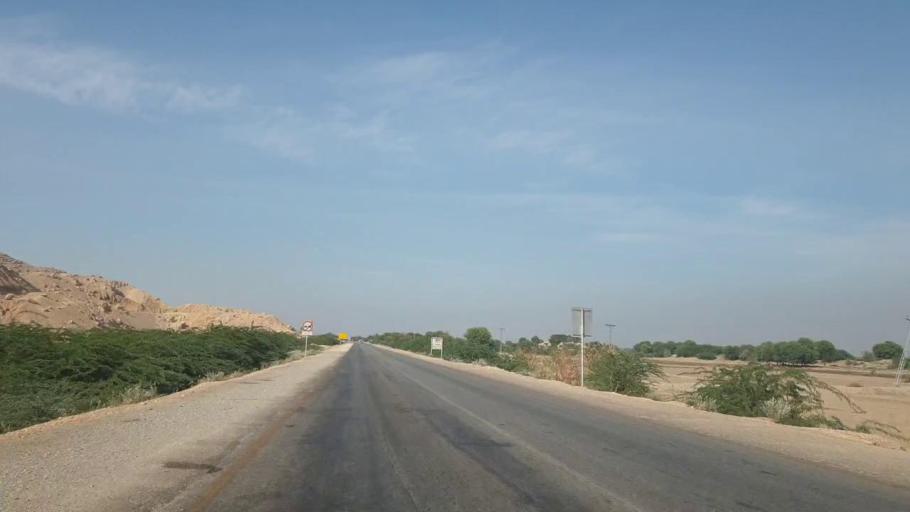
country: PK
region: Sindh
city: Sehwan
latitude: 26.3067
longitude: 67.8930
